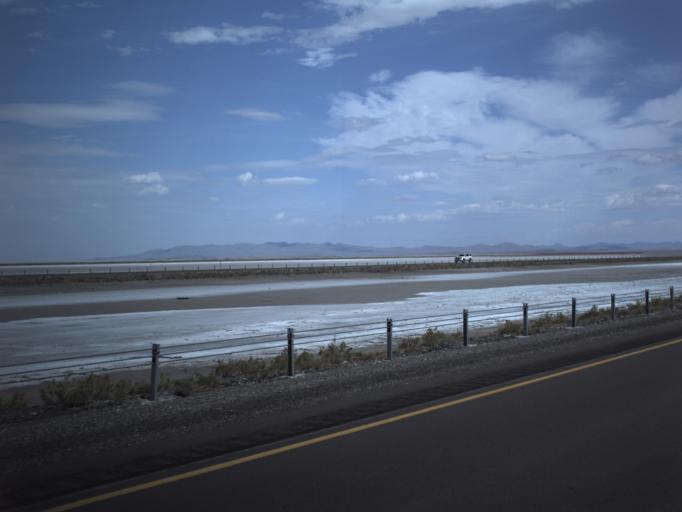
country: US
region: Utah
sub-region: Tooele County
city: Wendover
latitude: 40.7283
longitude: -113.3922
